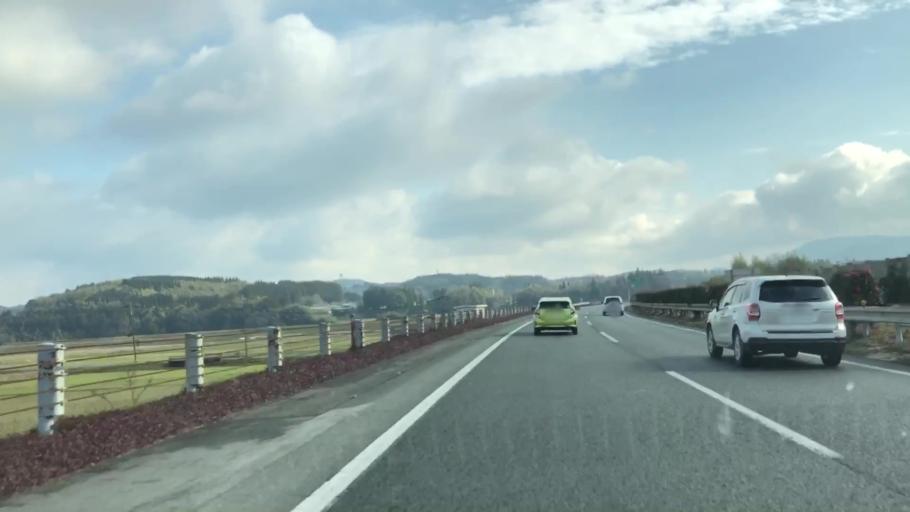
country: JP
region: Kumamoto
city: Tamana
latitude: 32.9952
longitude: 130.5987
